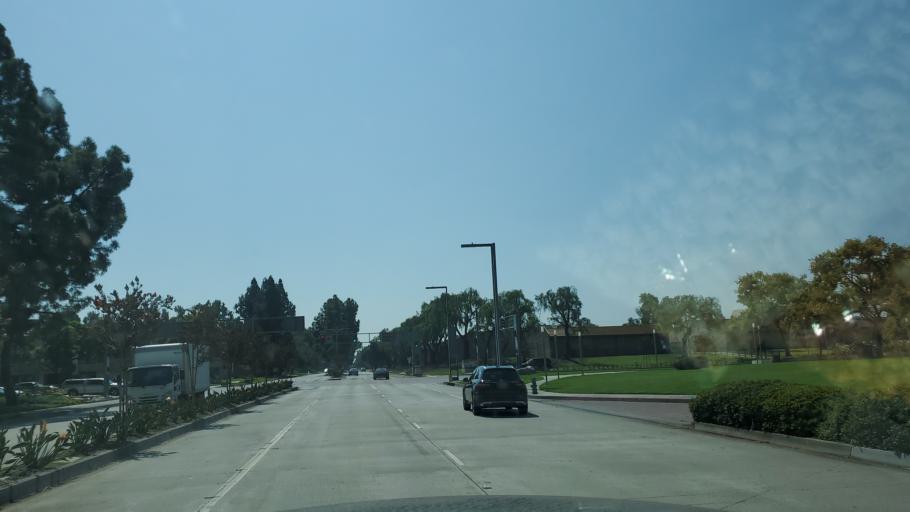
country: US
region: California
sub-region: Los Angeles County
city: Cerritos
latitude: 33.8667
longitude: -118.0638
